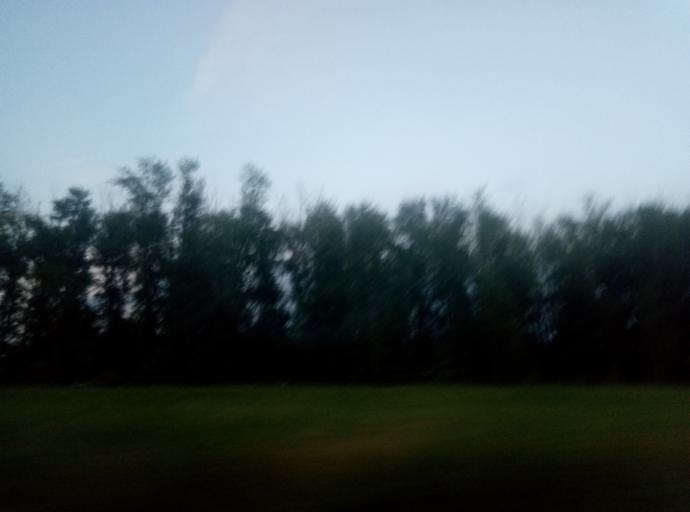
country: RU
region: Tula
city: Kireyevsk
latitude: 53.8520
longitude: 37.8775
